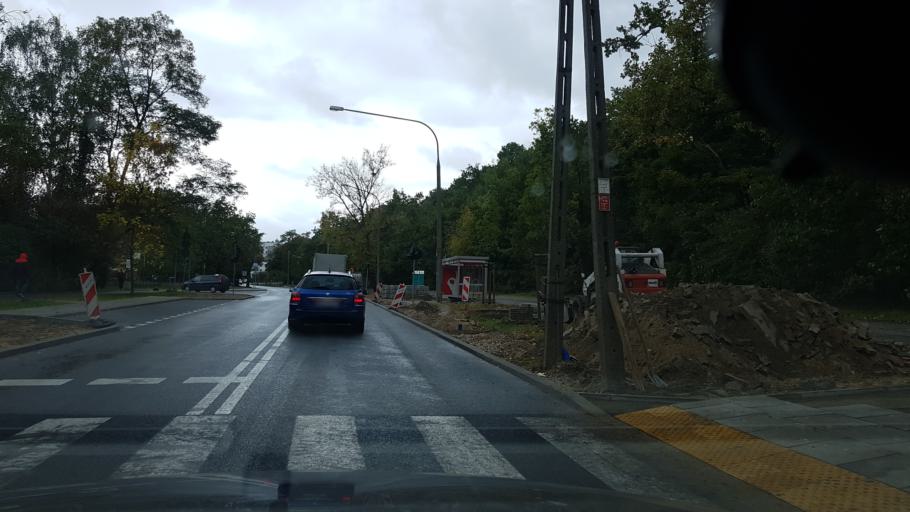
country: PL
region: Masovian Voivodeship
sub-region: Warszawa
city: Zoliborz
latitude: 52.2857
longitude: 20.9715
